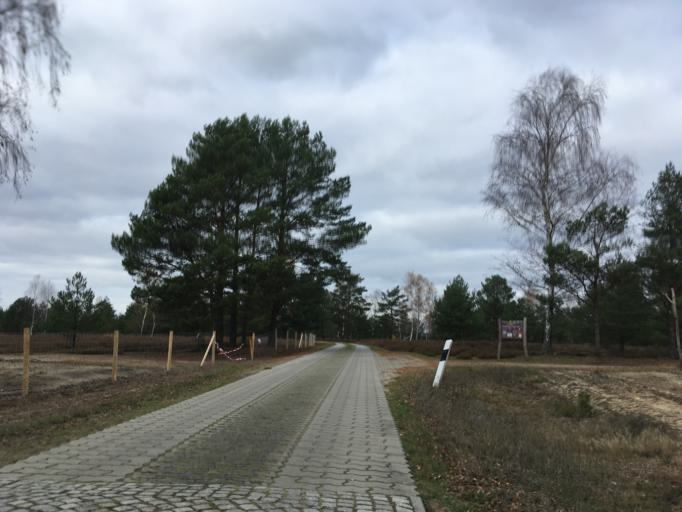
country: DE
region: Brandenburg
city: Tauer
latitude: 52.0062
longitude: 14.5001
